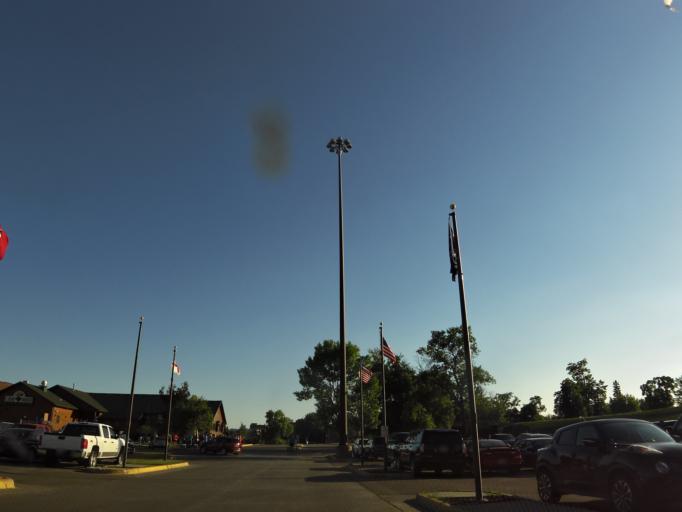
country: US
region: Minnesota
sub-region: Polk County
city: East Grand Forks
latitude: 47.9295
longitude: -97.0277
